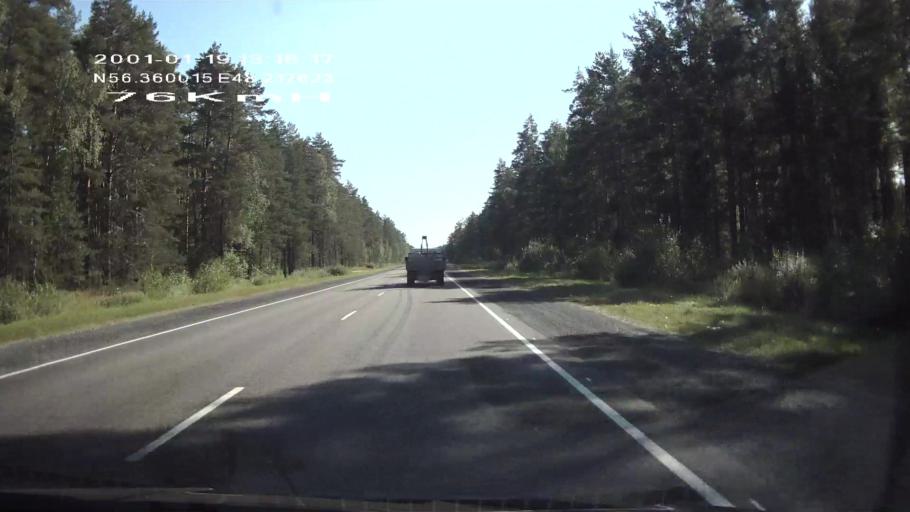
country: RU
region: Mariy-El
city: Suslonger
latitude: 56.3599
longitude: 48.2178
